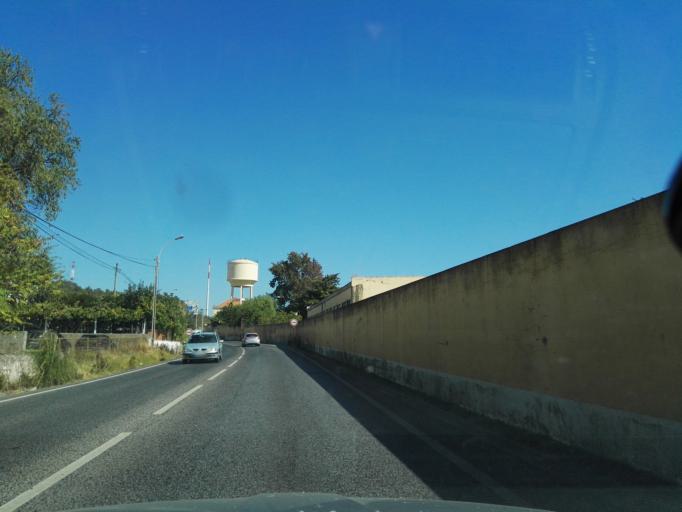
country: PT
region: Lisbon
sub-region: Vila Franca de Xira
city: Vila Franca de Xira
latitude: 38.9423
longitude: -8.9975
